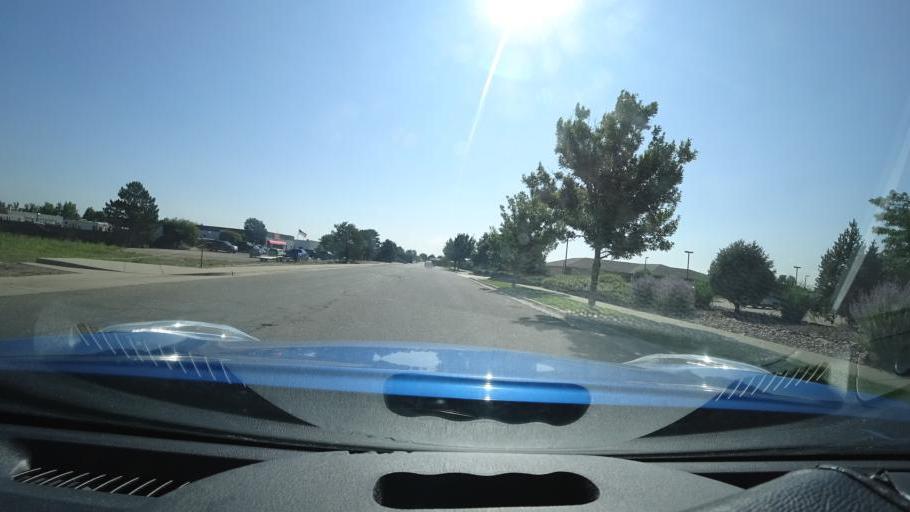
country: US
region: Colorado
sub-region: Adams County
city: Aurora
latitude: 39.7220
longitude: -104.8000
